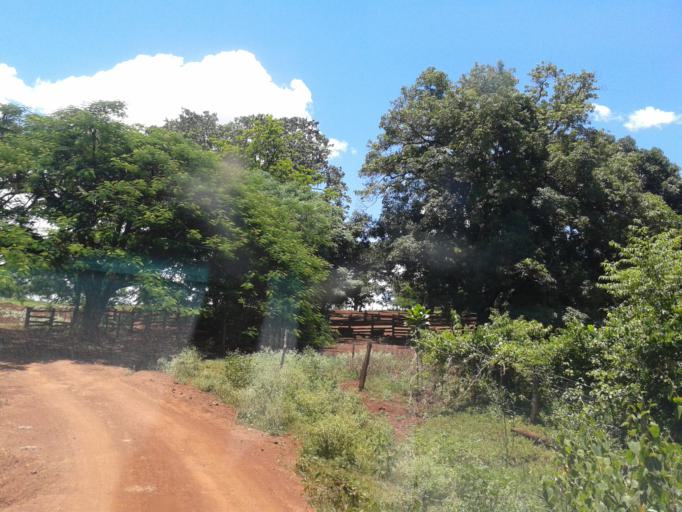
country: BR
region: Minas Gerais
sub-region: Centralina
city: Centralina
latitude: -18.7006
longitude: -49.1817
